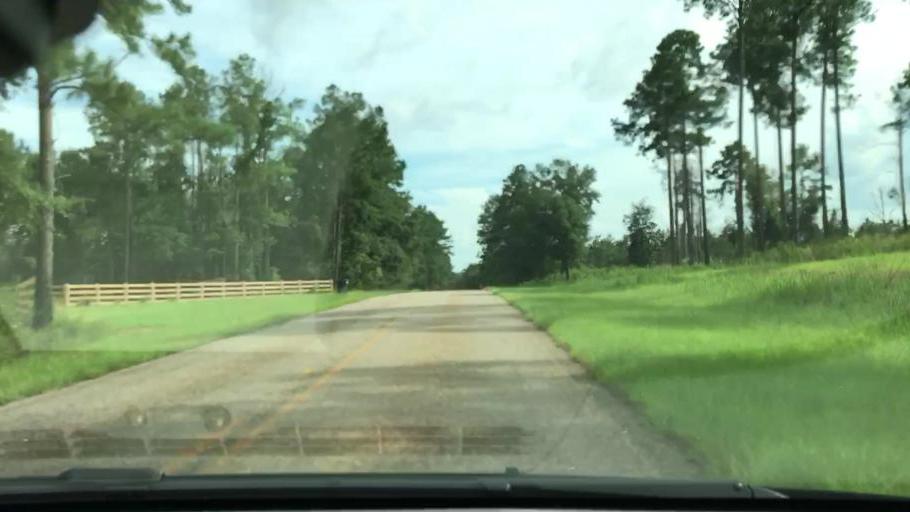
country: US
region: Georgia
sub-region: Clay County
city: Fort Gaines
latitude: 31.5138
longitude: -84.9533
